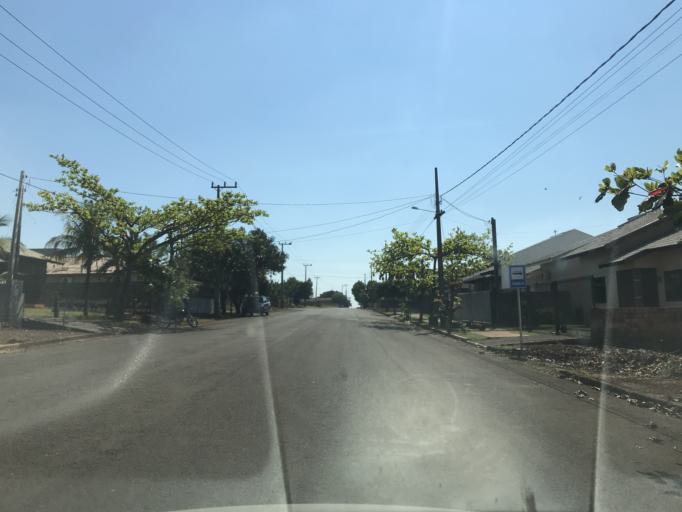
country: BR
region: Parana
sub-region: Palotina
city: Palotina
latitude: -24.2990
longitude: -53.8312
